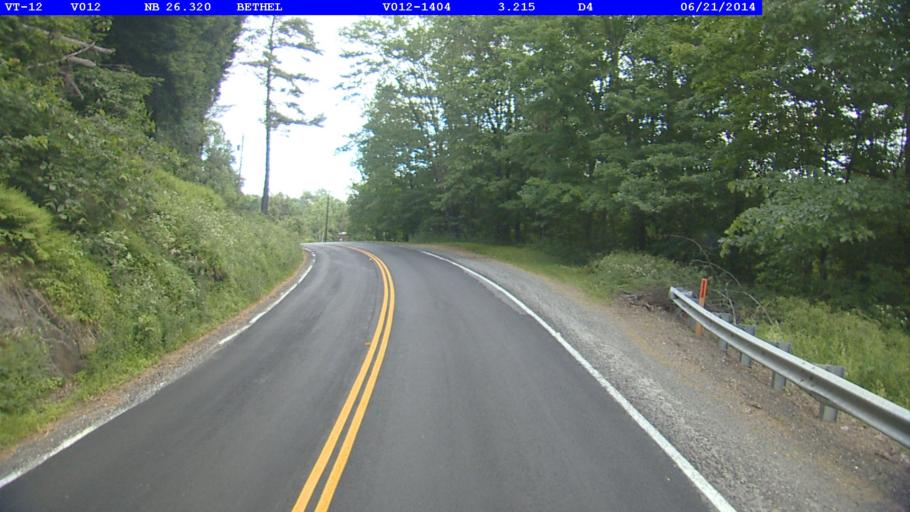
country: US
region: Vermont
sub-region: Orange County
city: Randolph
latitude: 43.8444
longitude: -72.6491
